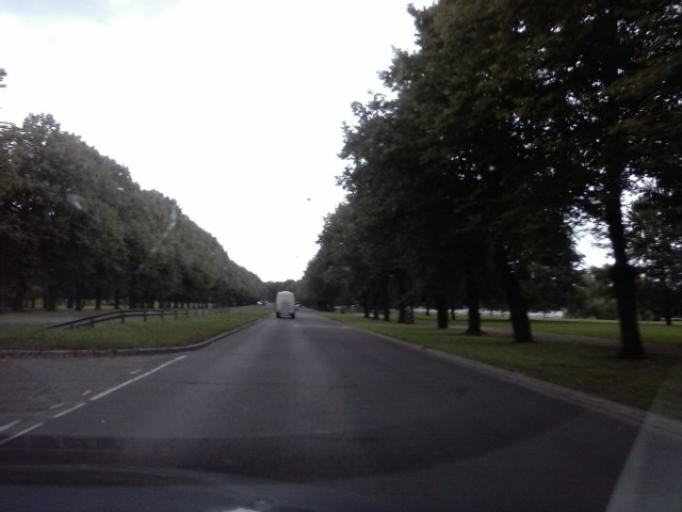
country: LV
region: Riga
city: Riga
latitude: 56.9368
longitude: 24.0807
